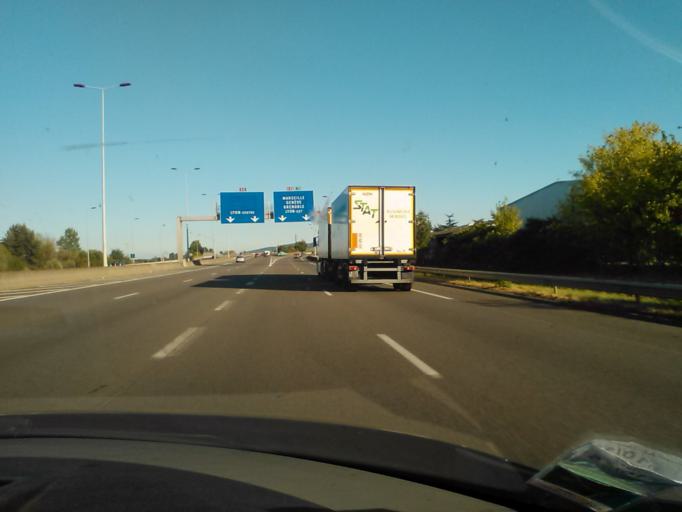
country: FR
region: Rhone-Alpes
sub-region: Departement du Rhone
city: Anse
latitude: 45.9410
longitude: 4.7216
